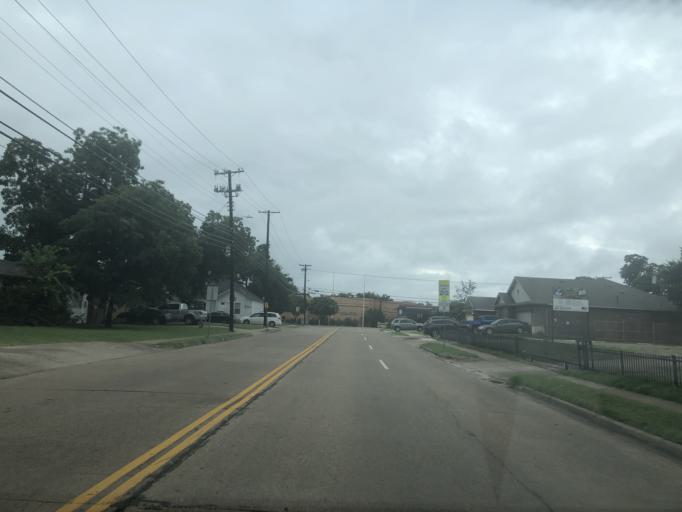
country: US
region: Texas
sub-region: Dallas County
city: Irving
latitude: 32.7949
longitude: -96.9469
